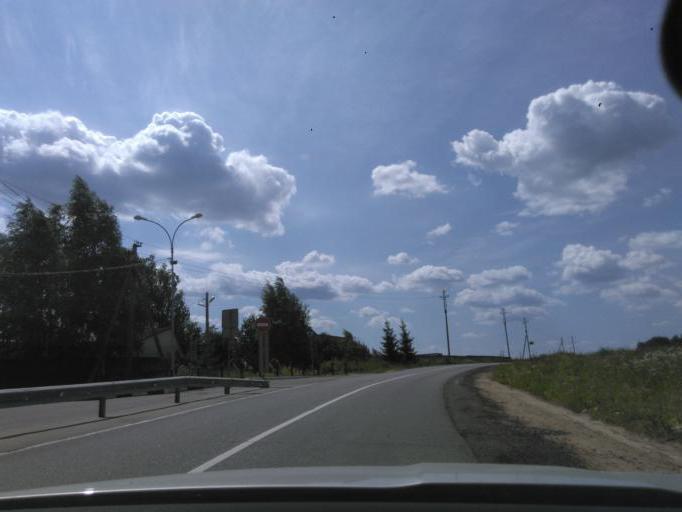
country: RU
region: Moskovskaya
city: Solnechnogorsk
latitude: 56.1486
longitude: 36.9802
